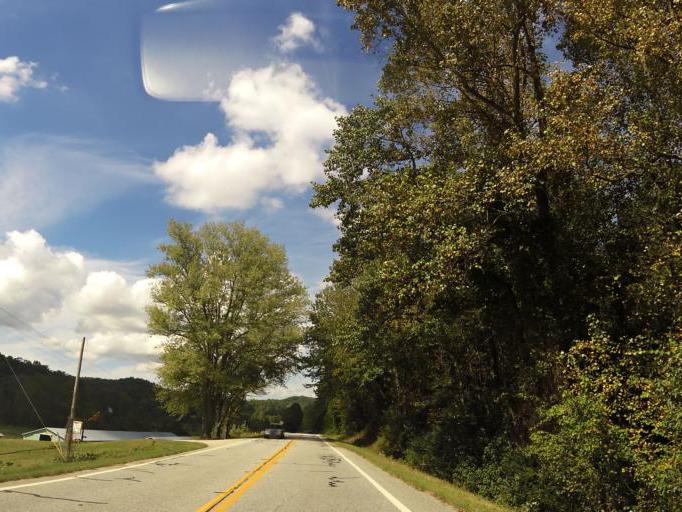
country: US
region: Georgia
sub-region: Dawson County
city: Dawsonville
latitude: 34.5338
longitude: -84.2564
